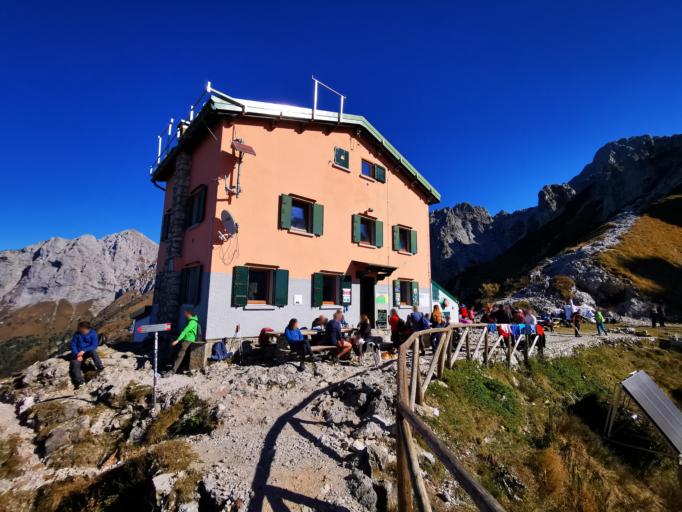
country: IT
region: Lombardy
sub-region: Provincia di Lecco
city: Abbadia Lariana
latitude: 45.9222
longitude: 9.3760
